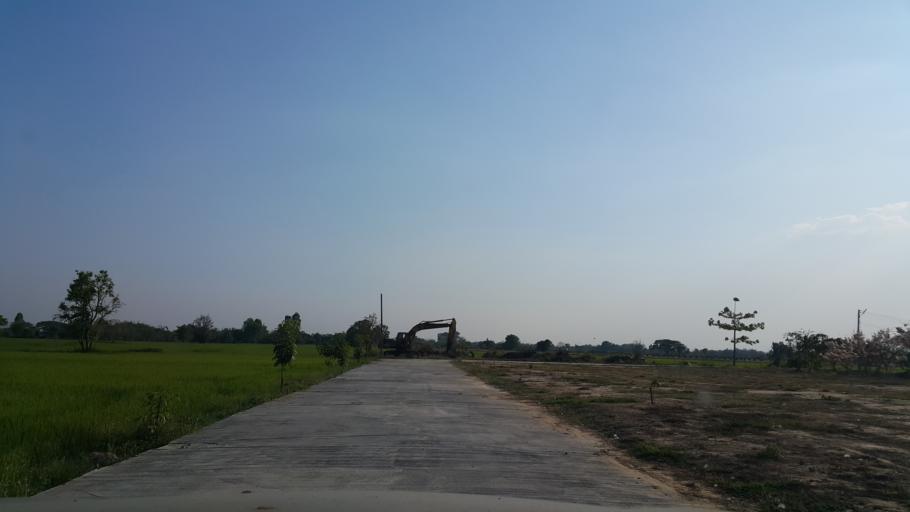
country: TH
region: Chiang Mai
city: San Sai
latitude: 18.8358
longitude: 99.0961
